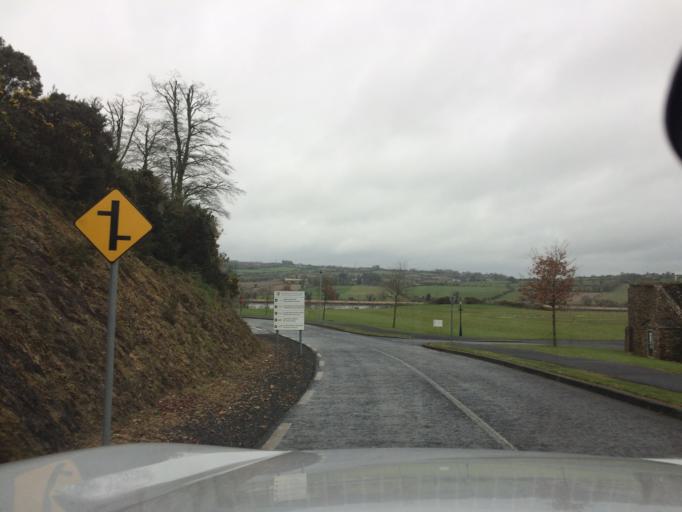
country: IE
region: Leinster
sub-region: Kilkenny
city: Mooncoin
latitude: 52.2538
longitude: -7.1862
